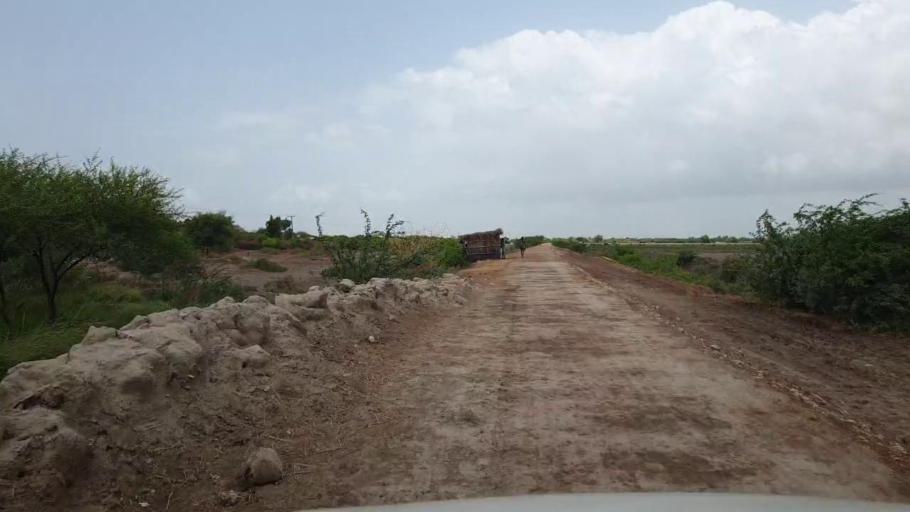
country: PK
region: Sindh
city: Kario
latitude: 24.6922
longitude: 68.6570
